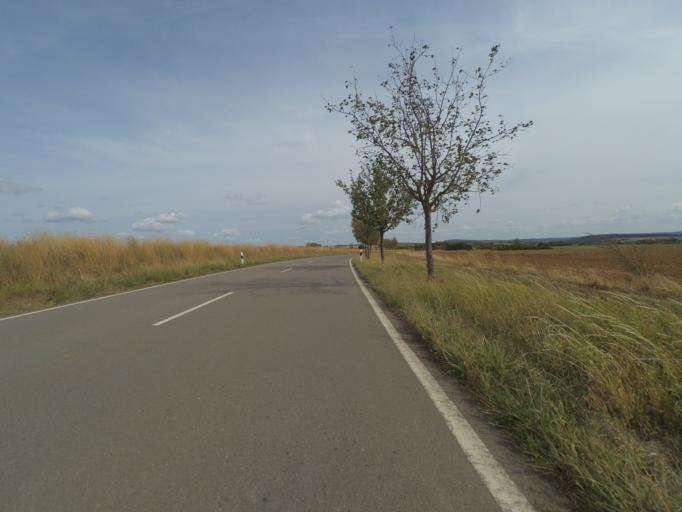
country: LU
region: Grevenmacher
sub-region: Canton de Remich
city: Mondorf-les-Bains
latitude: 49.4917
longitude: 6.3035
